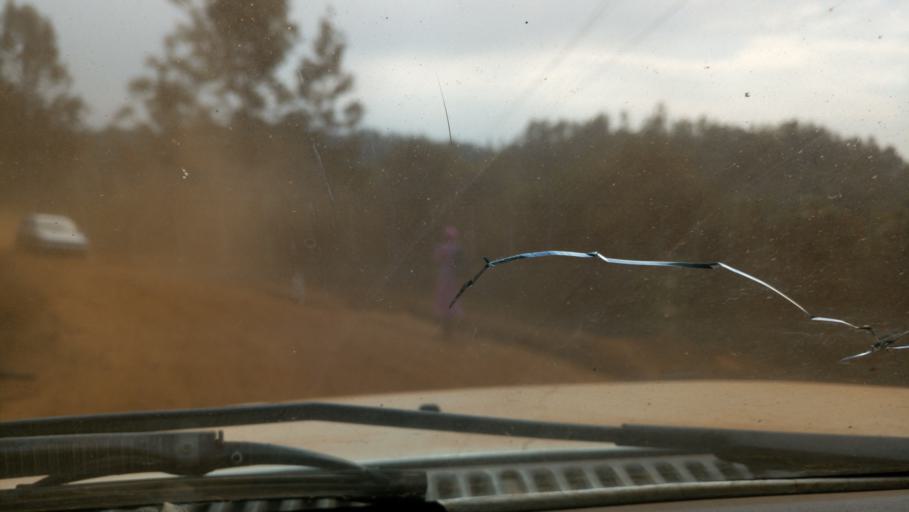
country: KE
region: Murang'a District
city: Kangema
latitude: -0.7459
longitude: 37.0056
